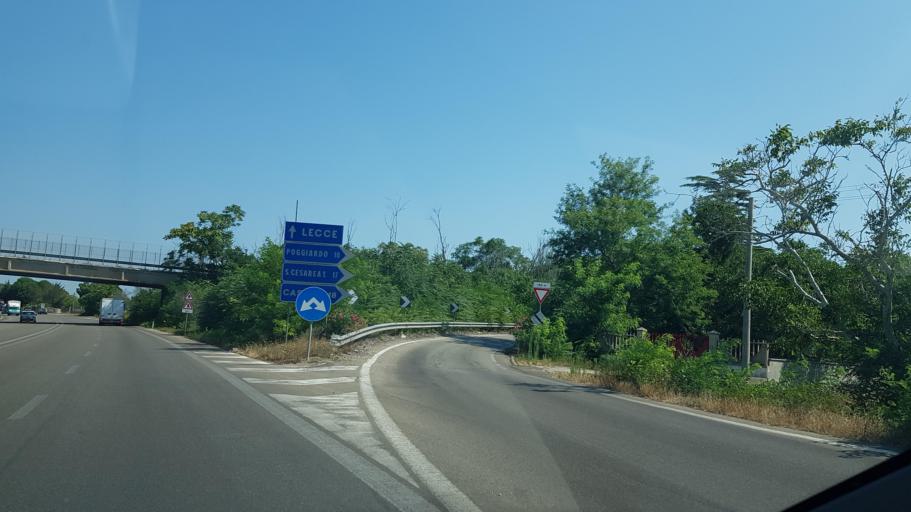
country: IT
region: Apulia
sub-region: Provincia di Lecce
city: Muro Leccese
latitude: 40.1158
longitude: 18.3209
